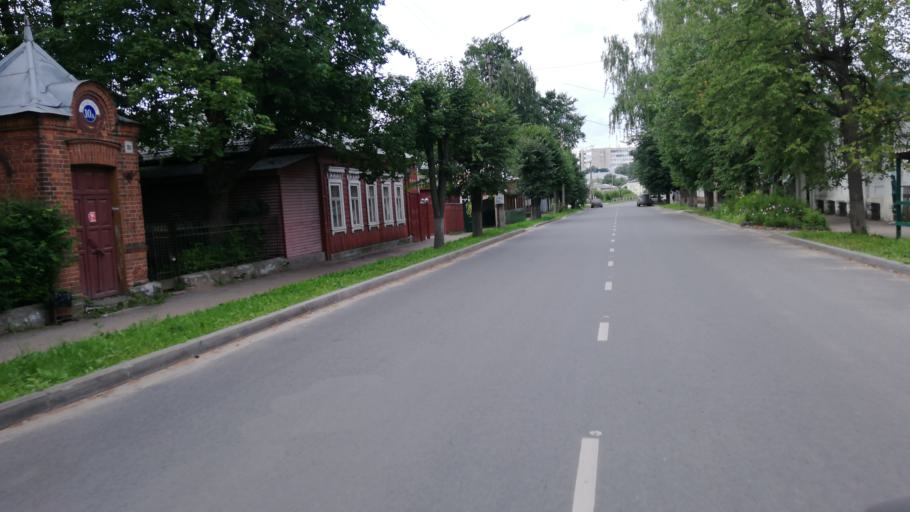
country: RU
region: Kostroma
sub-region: Kostromskoy Rayon
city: Kostroma
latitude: 57.7670
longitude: 40.9359
